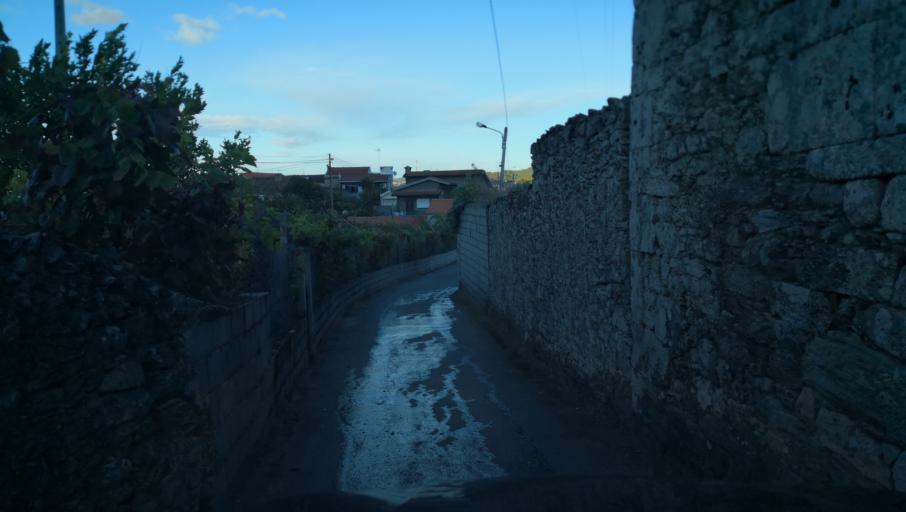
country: PT
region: Vila Real
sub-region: Vila Real
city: Vila Real
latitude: 41.2564
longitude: -7.7669
